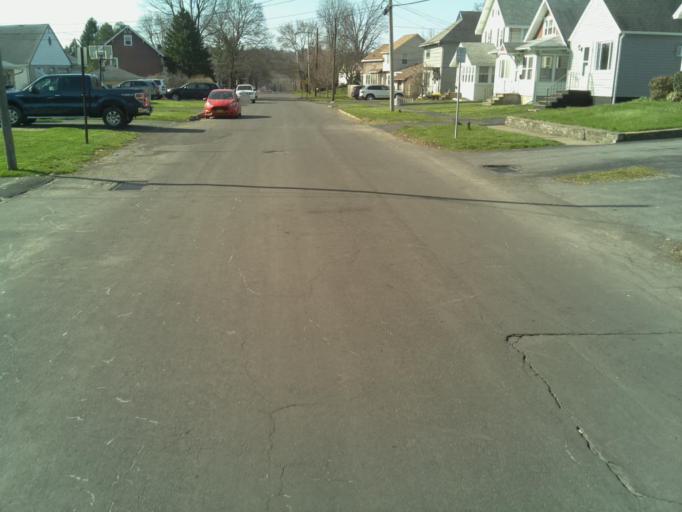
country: US
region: New York
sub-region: Onondaga County
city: East Syracuse
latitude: 43.0604
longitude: -76.1055
